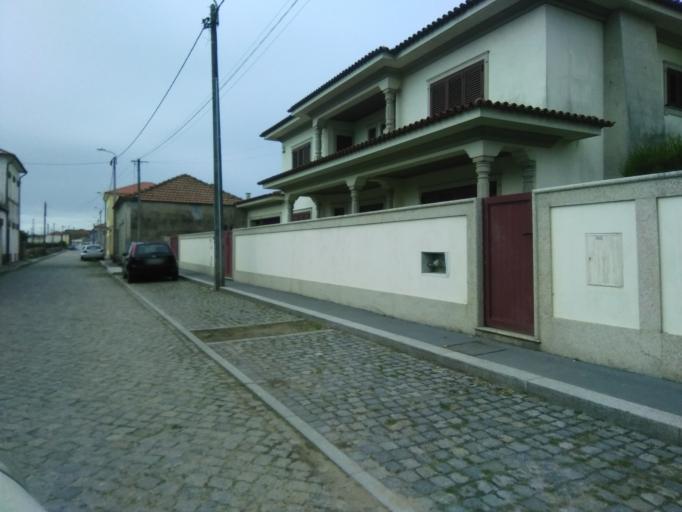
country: PT
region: Porto
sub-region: Matosinhos
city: Lavra
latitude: 41.2377
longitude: -8.7178
